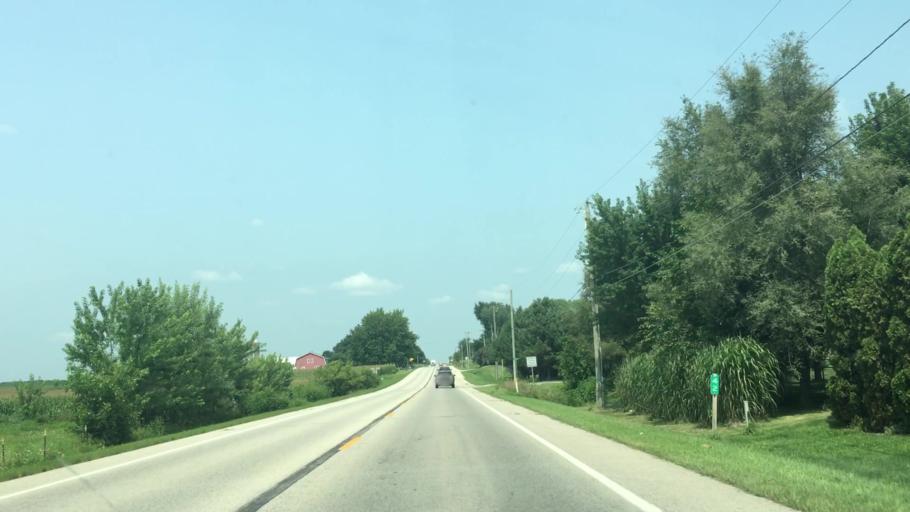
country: US
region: Iowa
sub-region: Buchanan County
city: Independence
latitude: 42.4844
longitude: -91.8894
